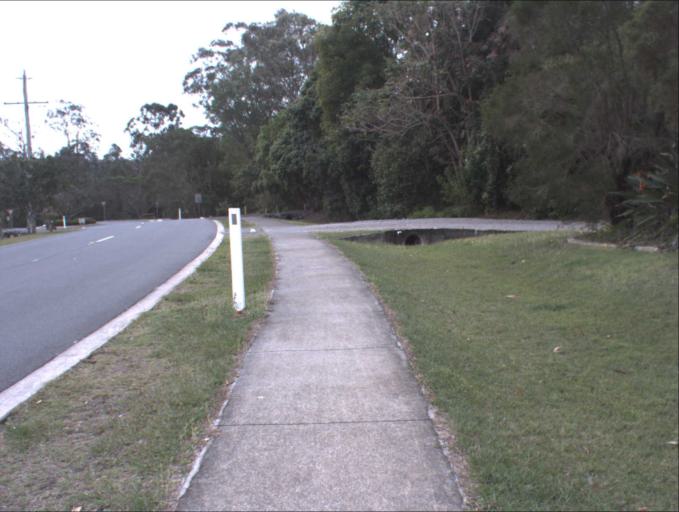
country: AU
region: Queensland
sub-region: Brisbane
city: Forest Lake
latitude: -27.6658
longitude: 152.9975
